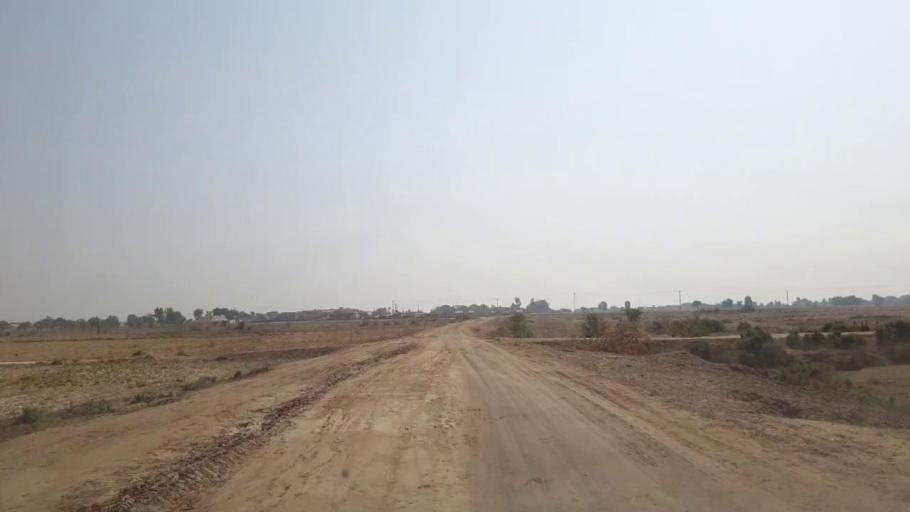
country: PK
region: Sindh
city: Mirpur Khas
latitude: 25.6419
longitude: 69.1444
